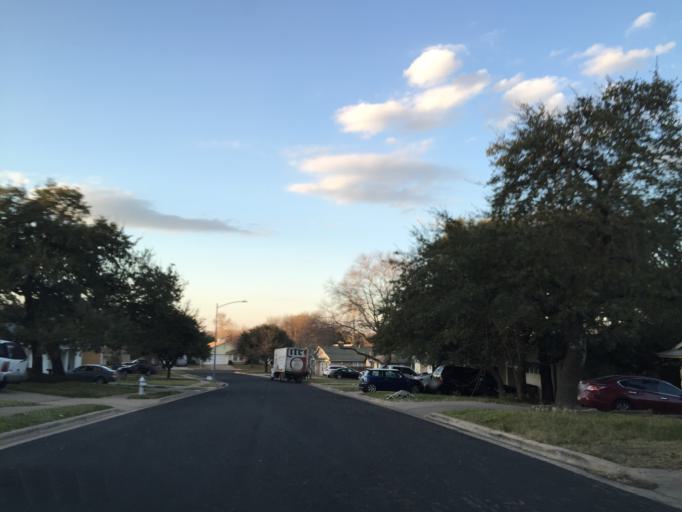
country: US
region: Texas
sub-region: Williamson County
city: Jollyville
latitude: 30.4372
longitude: -97.7413
